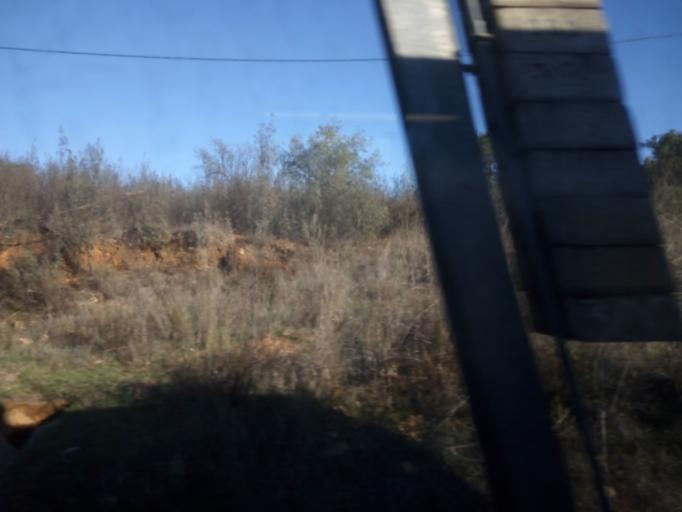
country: PT
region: Beja
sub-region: Odemira
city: Odemira
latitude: 37.4987
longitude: -8.4817
